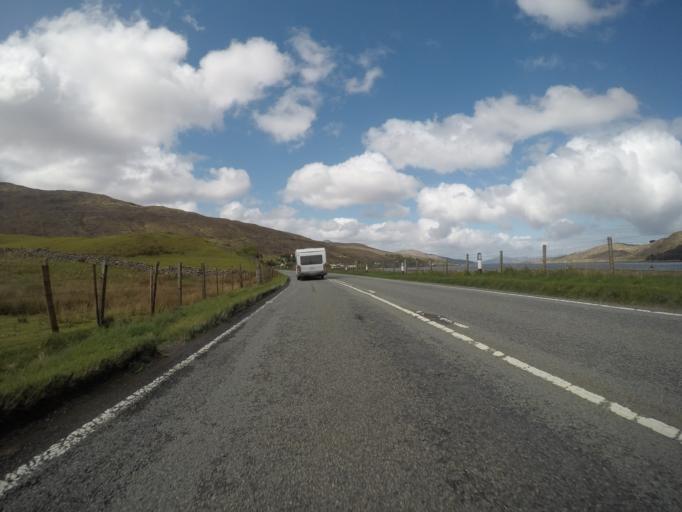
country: GB
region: Scotland
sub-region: Highland
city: Portree
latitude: 57.2698
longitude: -5.9890
